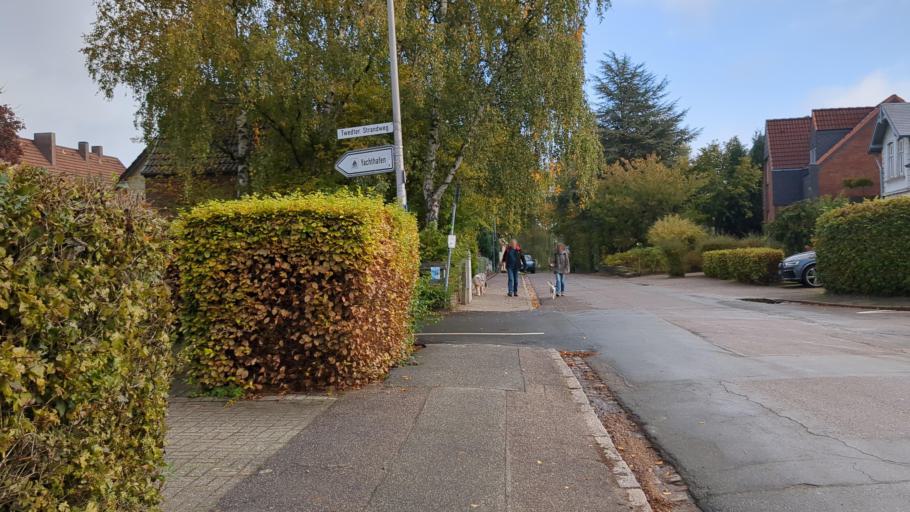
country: DE
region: Schleswig-Holstein
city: Wees
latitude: 54.8181
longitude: 9.4745
